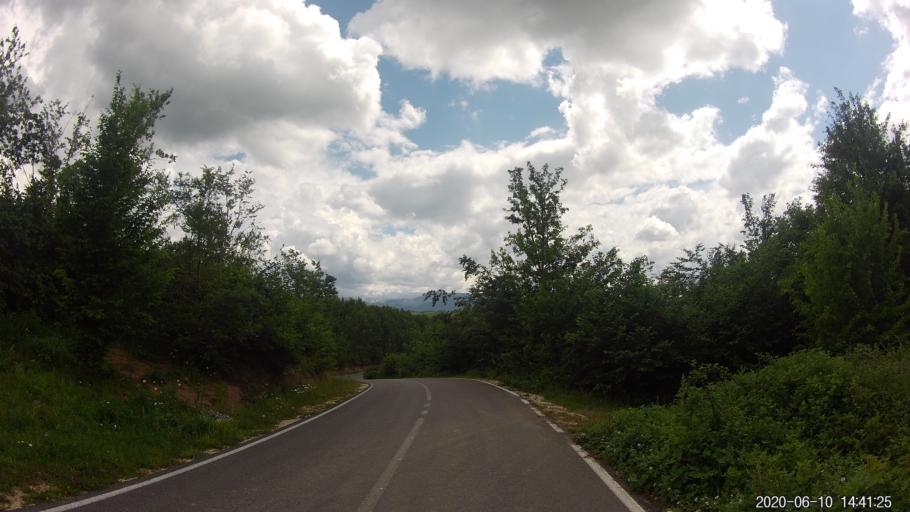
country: XK
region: Prizren
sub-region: Komuna e Therandes
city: Budakovo
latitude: 42.3905
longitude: 20.9443
